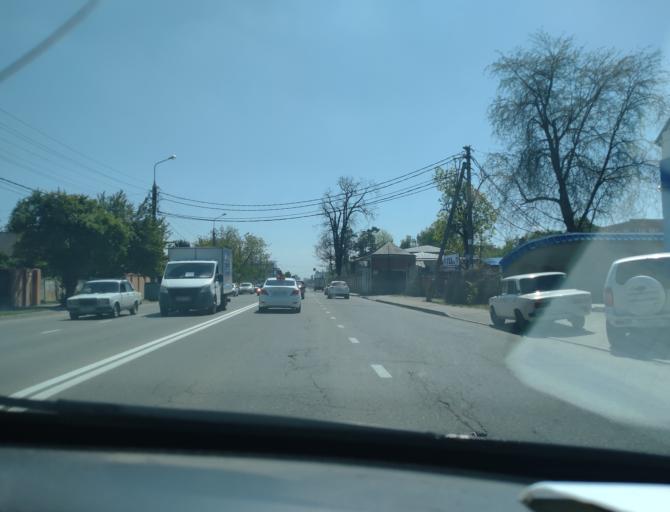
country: RU
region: Krasnodarskiy
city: Krasnodar
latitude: 45.0910
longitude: 39.0140
